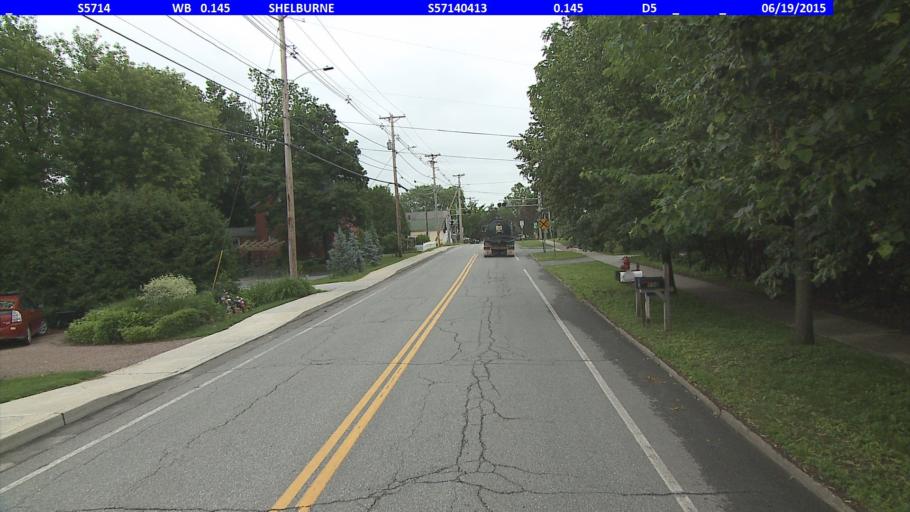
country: US
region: Vermont
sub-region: Chittenden County
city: Burlington
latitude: 44.3812
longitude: -73.2303
